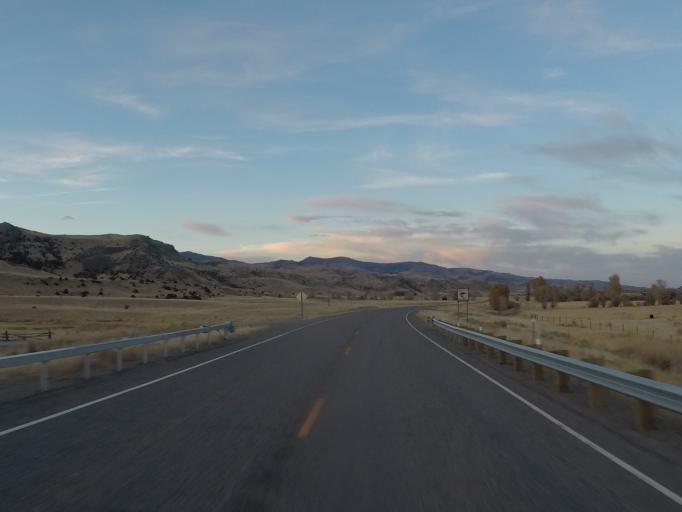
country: US
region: Montana
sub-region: Gallatin County
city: Bozeman
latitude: 45.2556
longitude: -110.8678
